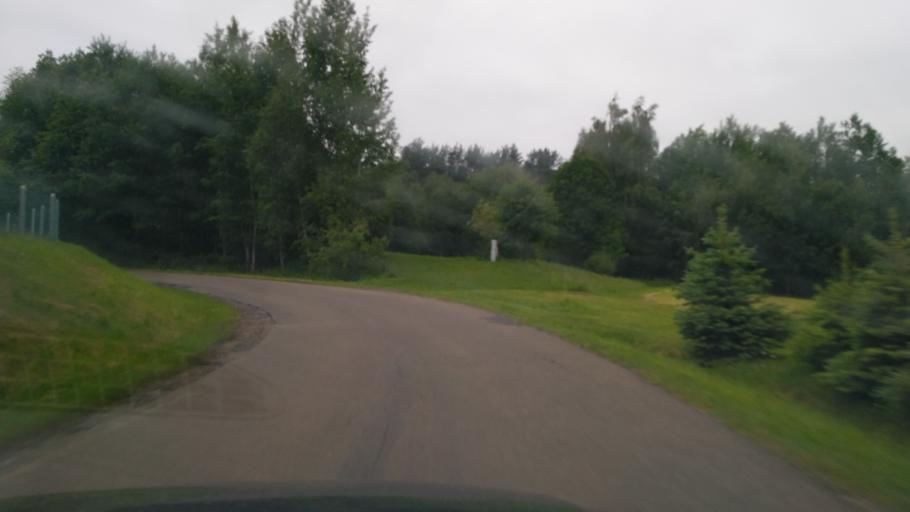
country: PL
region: Subcarpathian Voivodeship
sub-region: Powiat brzozowski
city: Orzechowka
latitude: 49.7278
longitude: 21.9328
